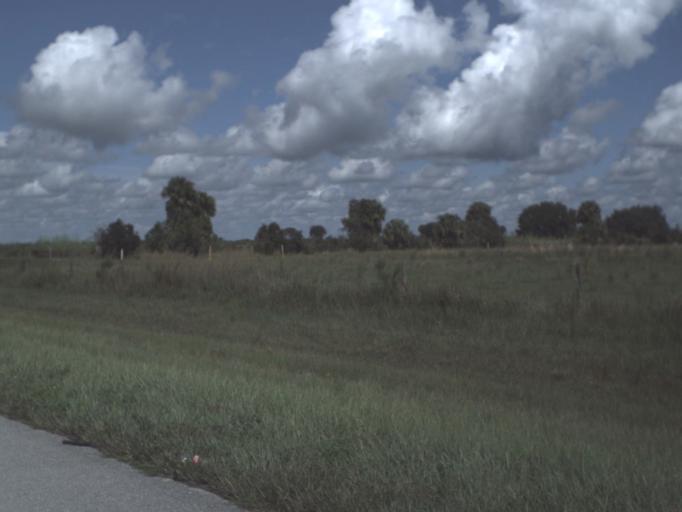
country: US
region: Florida
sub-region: Highlands County
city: Lake Placid
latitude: 27.4248
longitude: -81.2135
